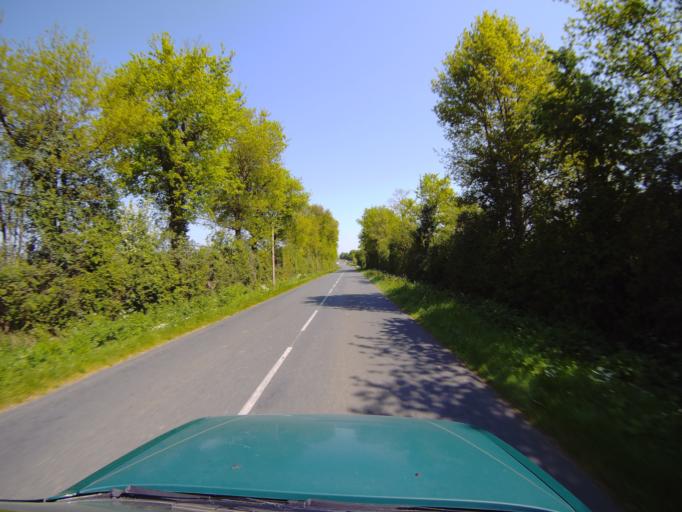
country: FR
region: Pays de la Loire
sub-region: Departement de la Vendee
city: Bouffere
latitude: 46.9485
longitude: -1.3587
